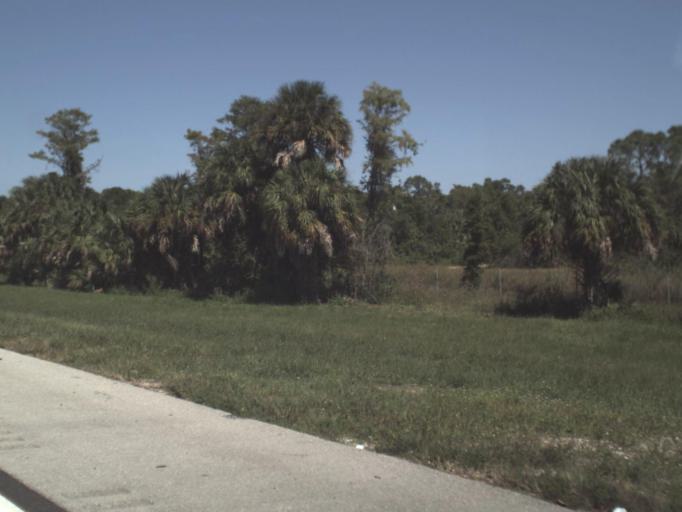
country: US
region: Florida
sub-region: Collier County
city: Vineyards
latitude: 26.2016
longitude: -81.7357
